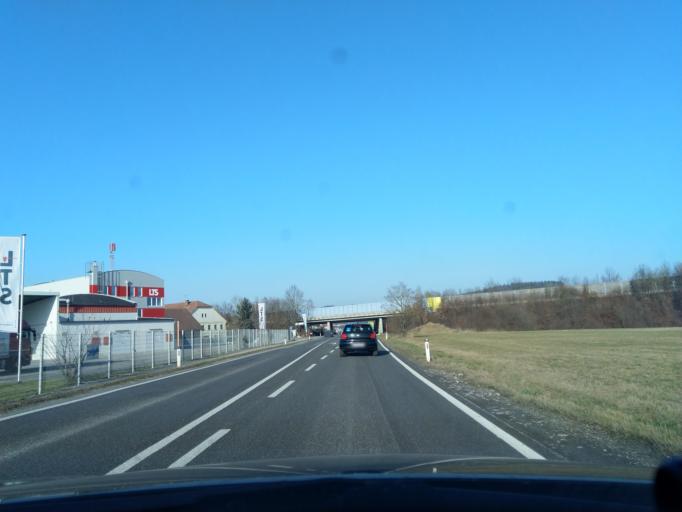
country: AT
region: Upper Austria
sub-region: Politischer Bezirk Scharding
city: Sankt Marienkirchen bei Schaerding
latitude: 48.3115
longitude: 13.4236
